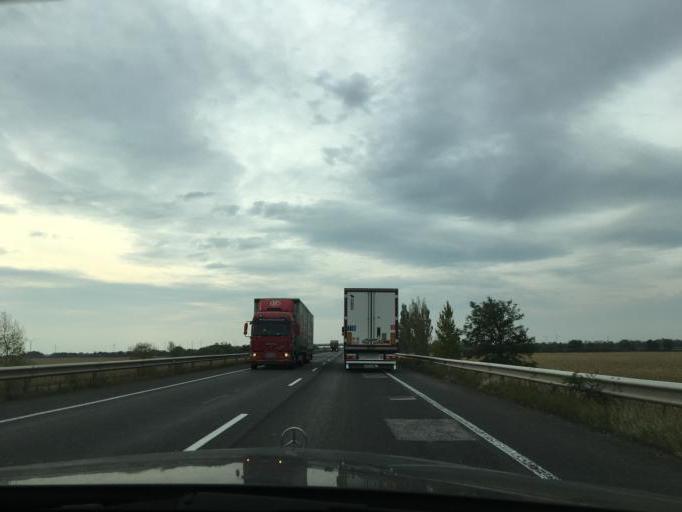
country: HU
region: Gyor-Moson-Sopron
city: Rajka
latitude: 47.9278
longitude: 17.1722
